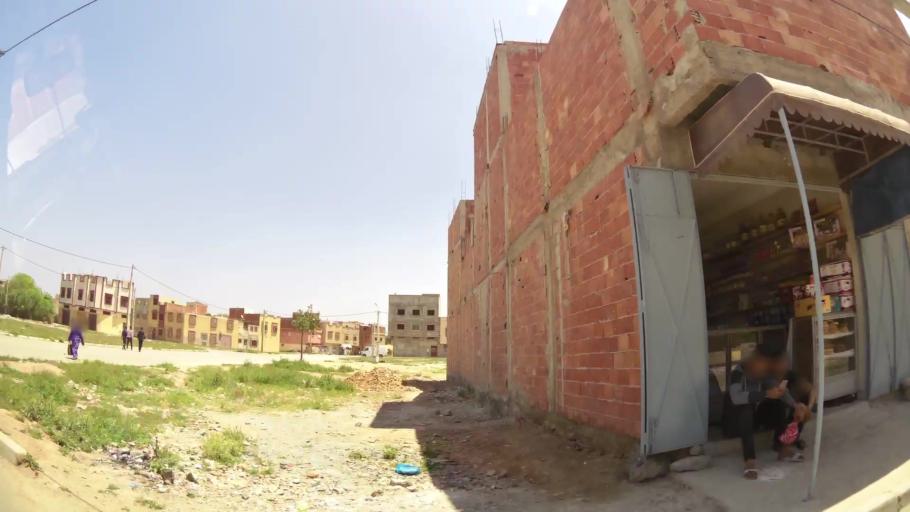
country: MA
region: Oriental
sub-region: Oujda-Angad
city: Oujda
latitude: 34.6814
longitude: -1.8979
